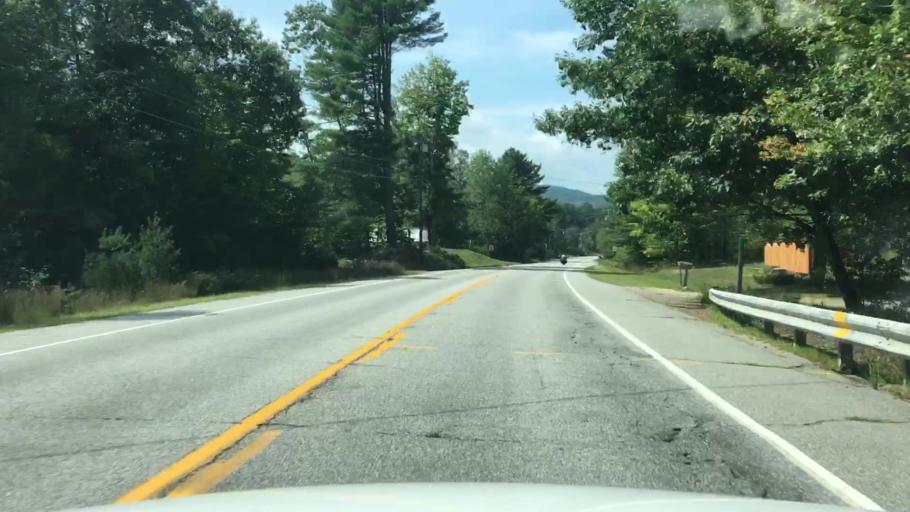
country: US
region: Maine
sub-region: Oxford County
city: Peru
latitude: 44.4862
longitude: -70.3694
